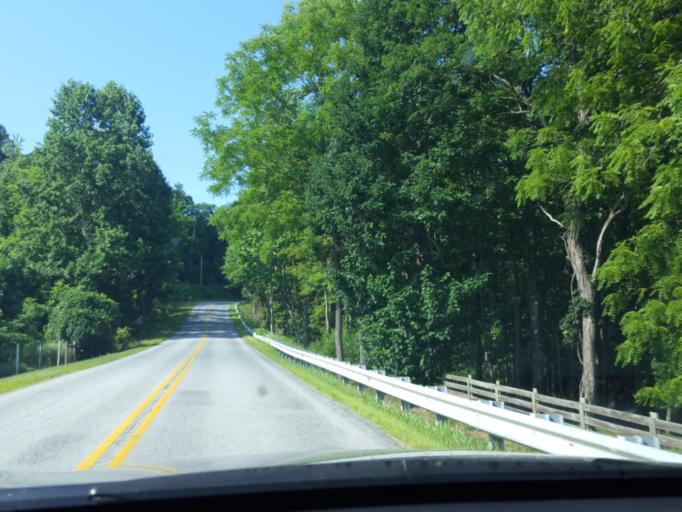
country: US
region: Virginia
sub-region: Nelson County
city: Nellysford
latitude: 37.9145
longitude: -78.9875
